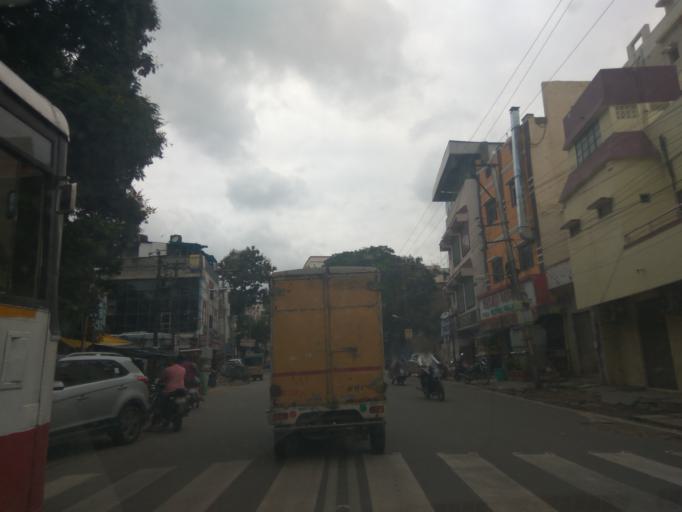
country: IN
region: Telangana
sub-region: Hyderabad
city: Hyderabad
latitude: 17.3960
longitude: 78.4878
